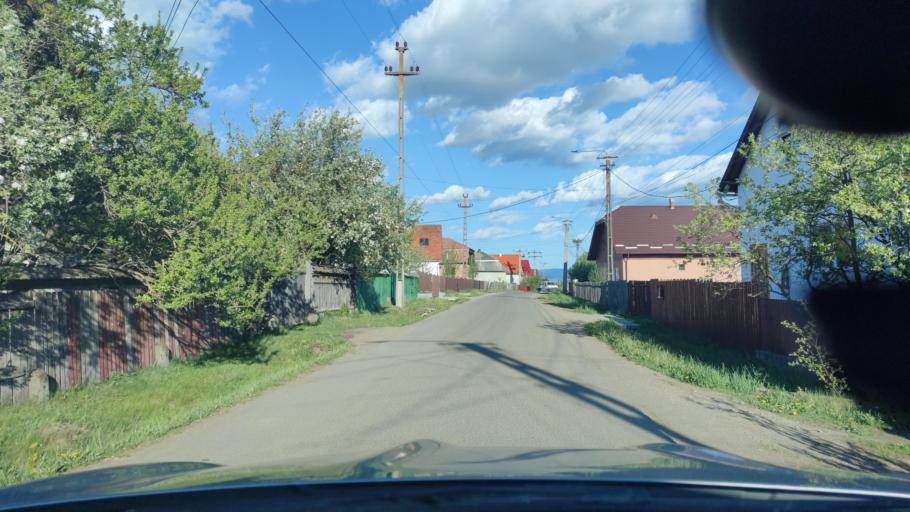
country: RO
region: Harghita
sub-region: Comuna Remetea
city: Remetea
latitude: 46.7990
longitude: 25.4319
